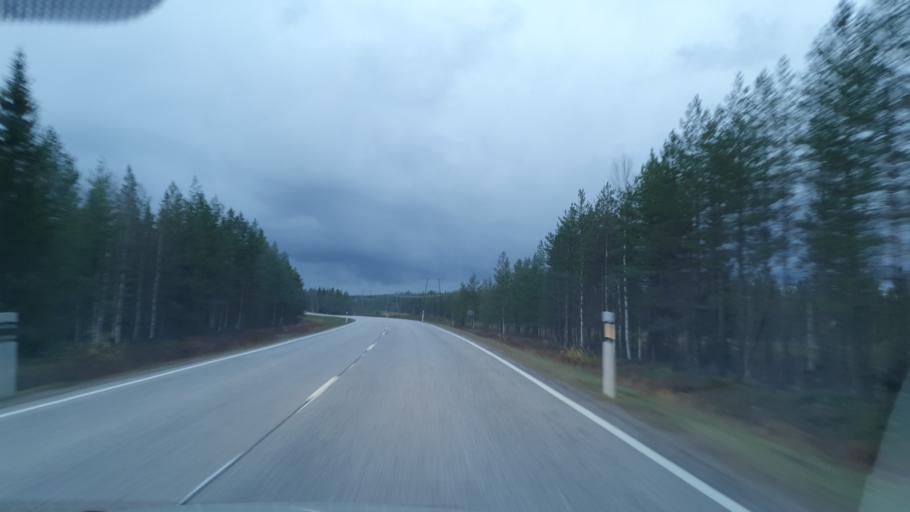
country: FI
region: Kainuu
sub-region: Kehys-Kainuu
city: Hyrynsalmi
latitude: 64.6183
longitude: 28.4773
